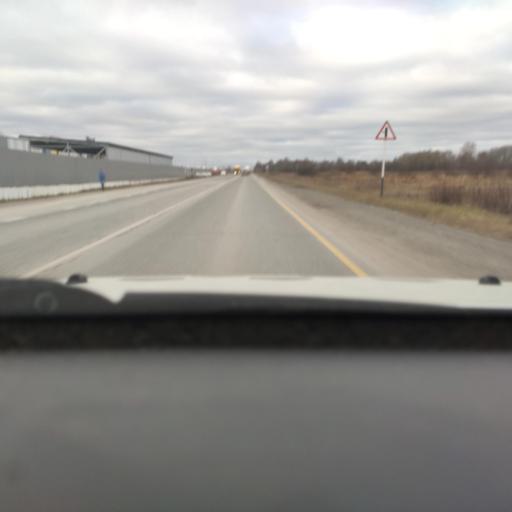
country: RU
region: Perm
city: Froly
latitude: 57.8963
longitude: 56.2538
